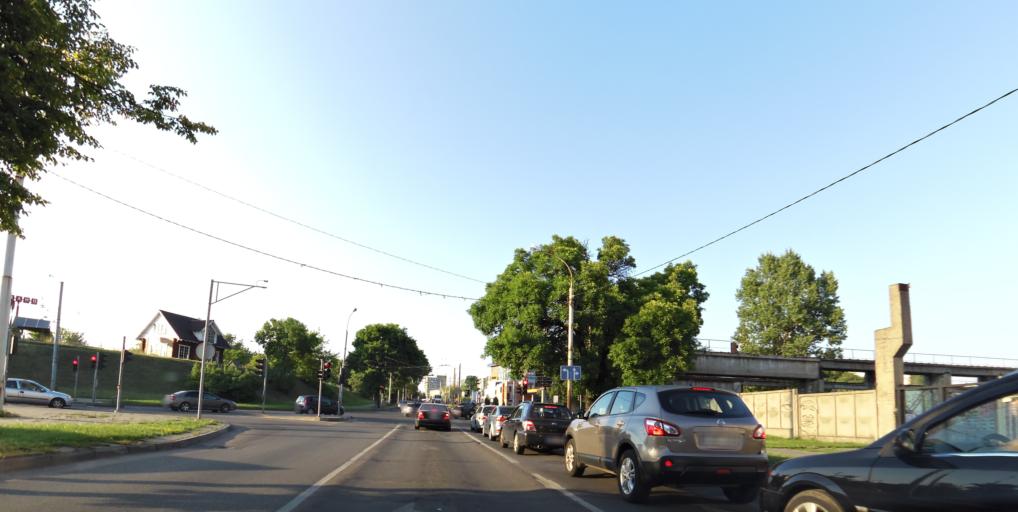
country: LT
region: Vilnius County
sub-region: Vilnius
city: Vilnius
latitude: 54.7167
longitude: 25.2946
